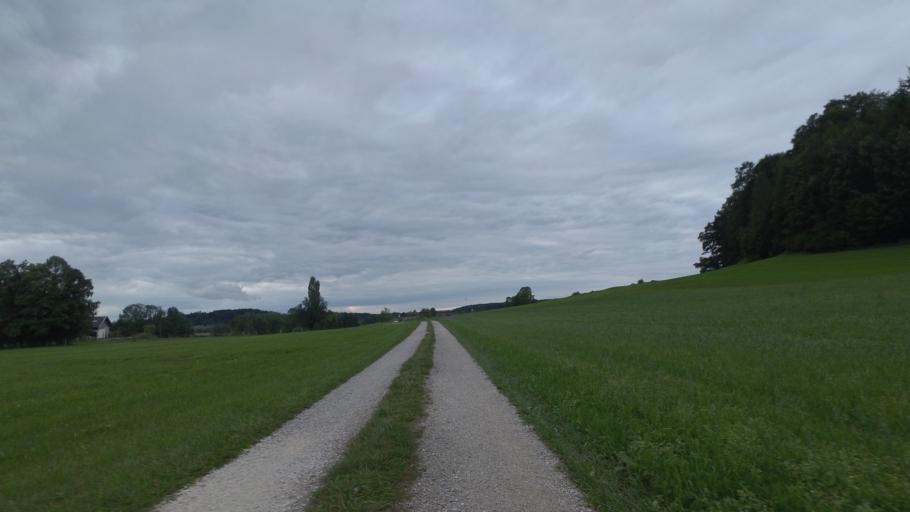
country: DE
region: Bavaria
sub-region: Upper Bavaria
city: Nussdorf
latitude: 47.9077
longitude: 12.5712
